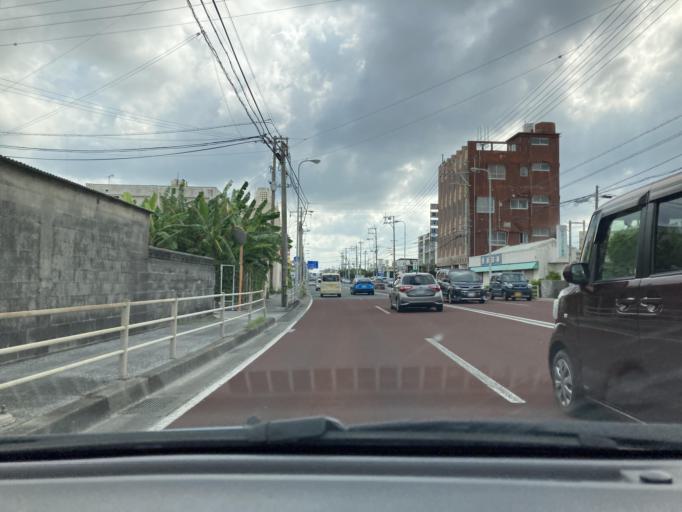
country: JP
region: Okinawa
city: Ginowan
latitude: 26.2143
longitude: 127.7619
